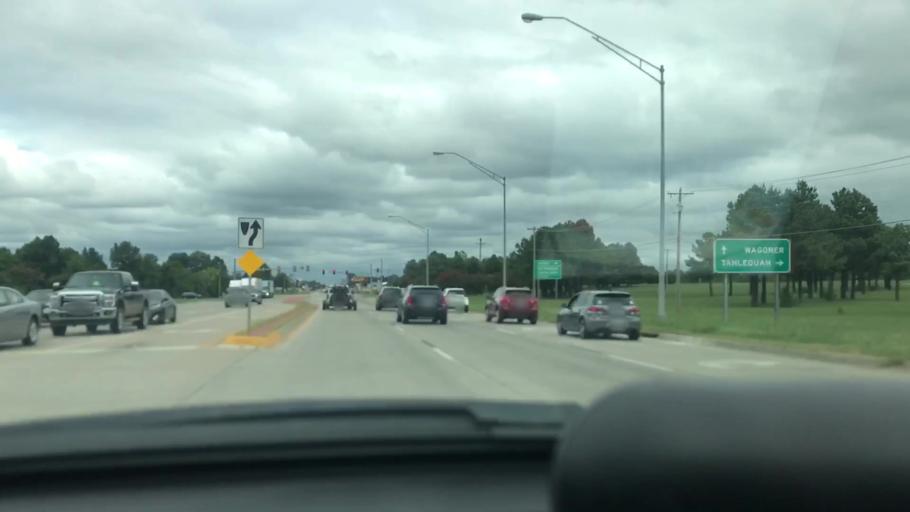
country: US
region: Oklahoma
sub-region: Muskogee County
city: Muskogee
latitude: 35.7674
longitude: -95.4024
